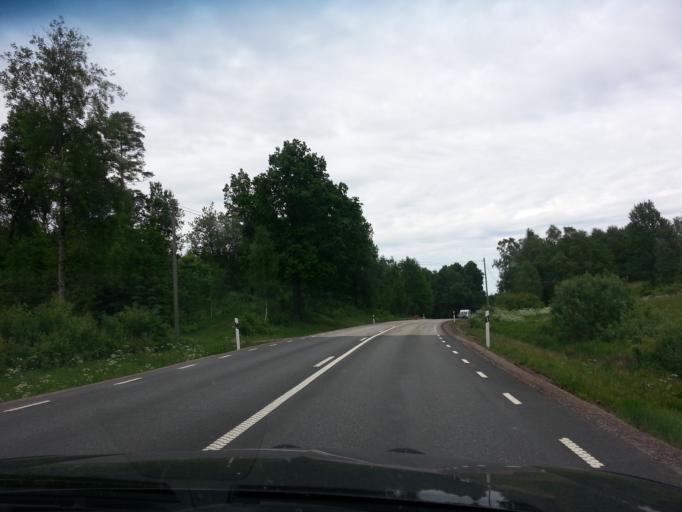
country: SE
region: Joenkoeping
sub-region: Vetlanda Kommun
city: Vetlanda
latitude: 57.2787
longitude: 15.1289
